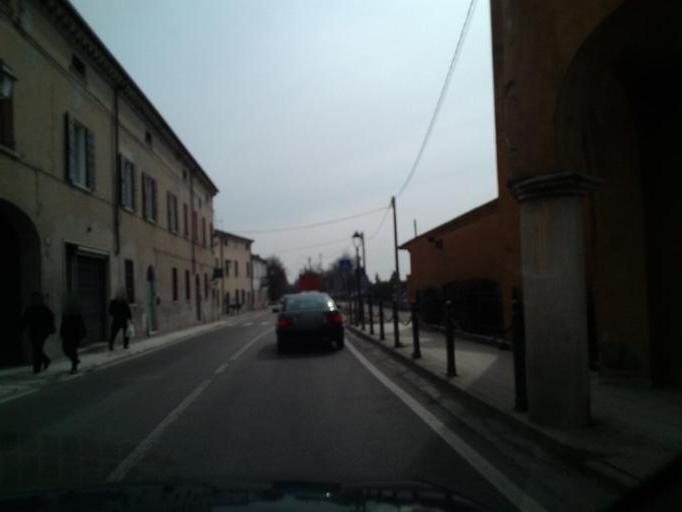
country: IT
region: Lombardy
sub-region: Provincia di Mantova
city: Roverbella
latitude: 45.2653
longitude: 10.7686
